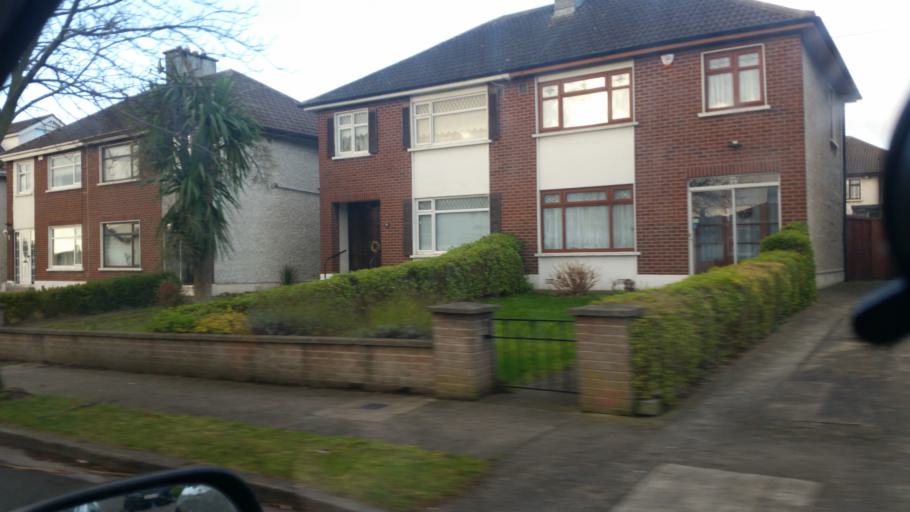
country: IE
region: Leinster
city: Artane
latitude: 53.3828
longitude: -6.2250
